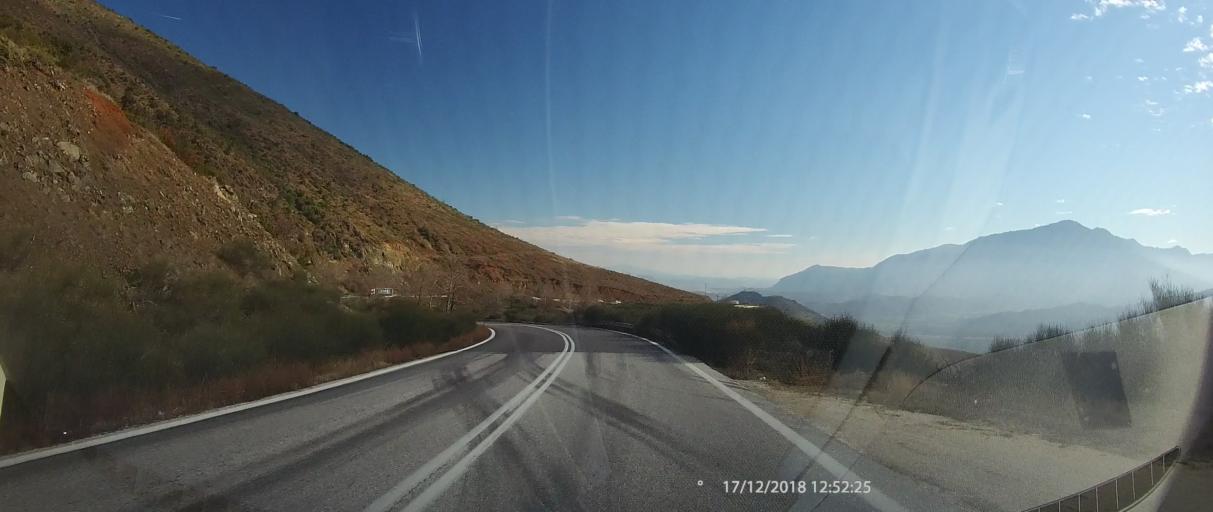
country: GR
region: Thessaly
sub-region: Trikala
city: Kastraki
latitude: 39.7589
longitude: 21.4778
